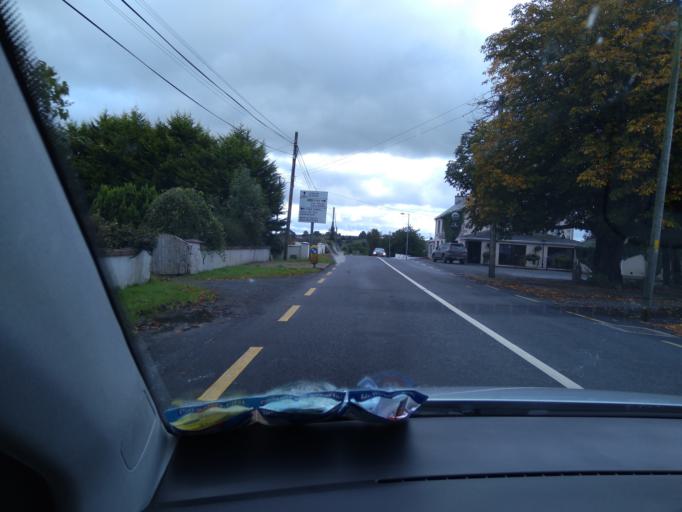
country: IE
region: Connaught
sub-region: Sligo
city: Collooney
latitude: 54.1926
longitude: -8.4471
